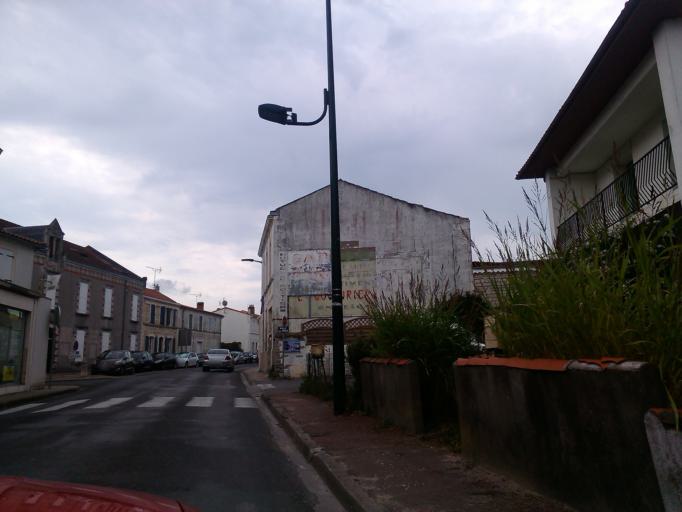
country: FR
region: Poitou-Charentes
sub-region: Departement de la Charente-Maritime
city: La Tremblade
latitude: 45.7676
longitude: -1.1408
